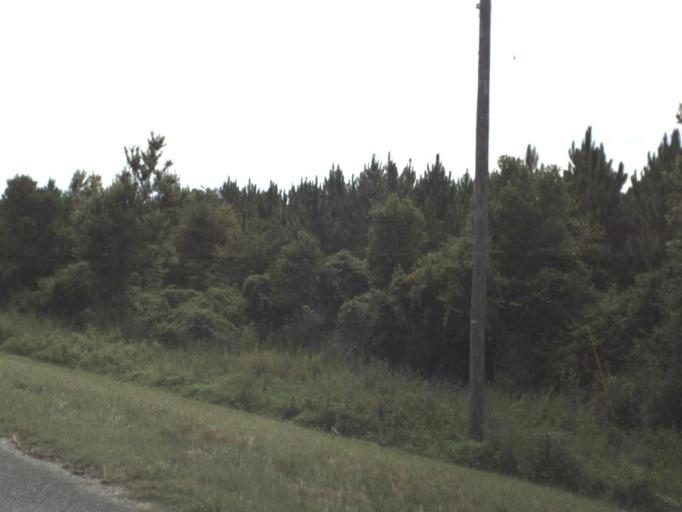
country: US
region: Florida
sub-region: Taylor County
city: Perry
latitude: 30.0926
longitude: -83.4916
